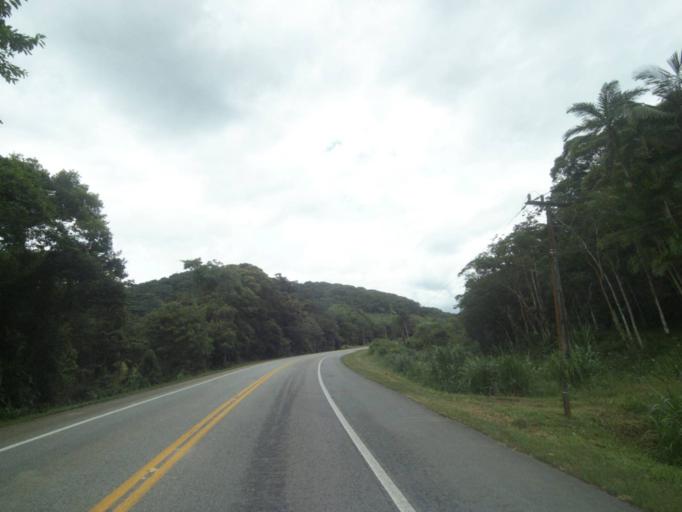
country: BR
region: Parana
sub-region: Antonina
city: Antonina
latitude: -25.4490
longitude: -48.7757
